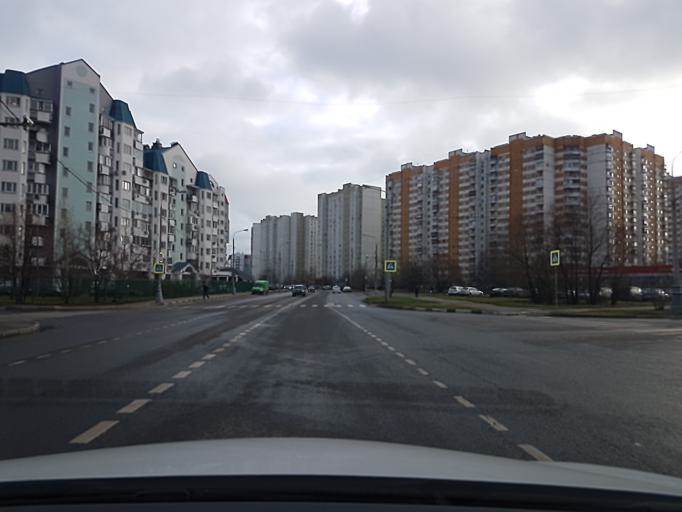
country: RU
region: Moskovskaya
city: Pavshino
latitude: 55.8381
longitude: 37.3520
